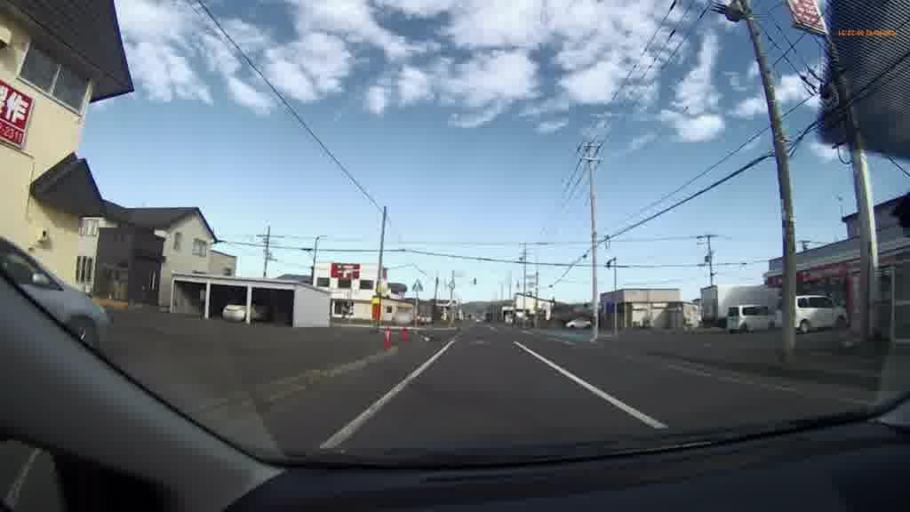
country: JP
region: Hokkaido
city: Kushiro
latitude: 42.9630
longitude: 144.0722
